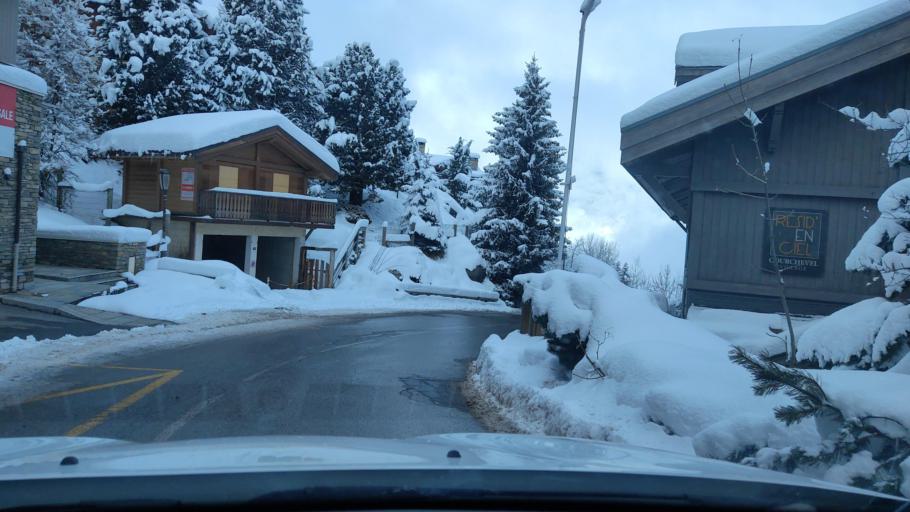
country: FR
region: Rhone-Alpes
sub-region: Departement de la Savoie
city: Courchevel
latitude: 45.4230
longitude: 6.6425
